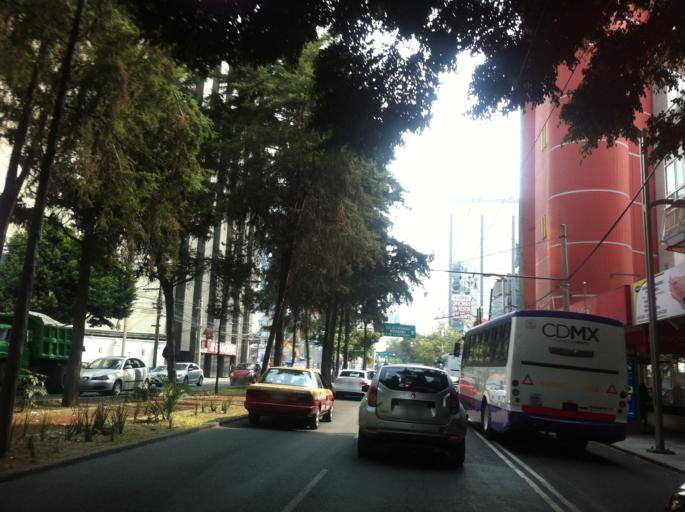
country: MX
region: Mexico City
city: Miguel Hidalgo
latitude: 19.4324
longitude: -99.1815
